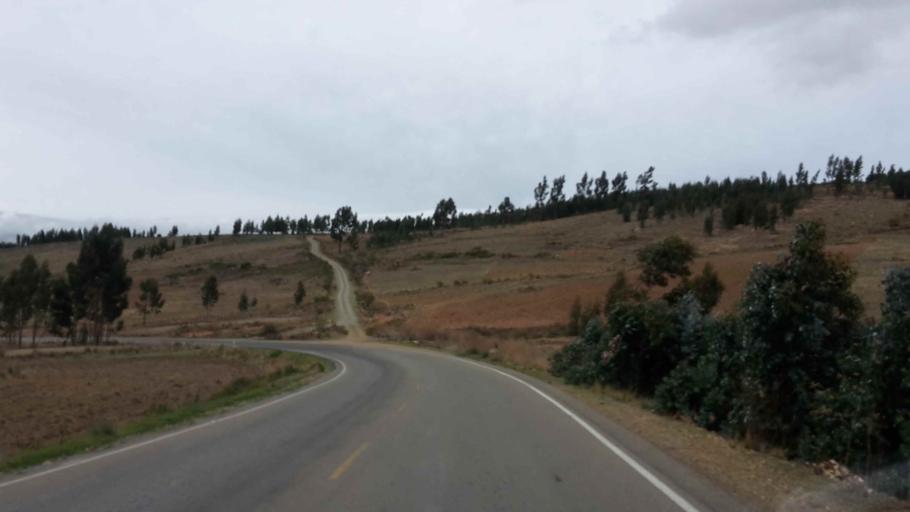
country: BO
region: Cochabamba
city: Arani
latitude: -17.4635
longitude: -65.6980
